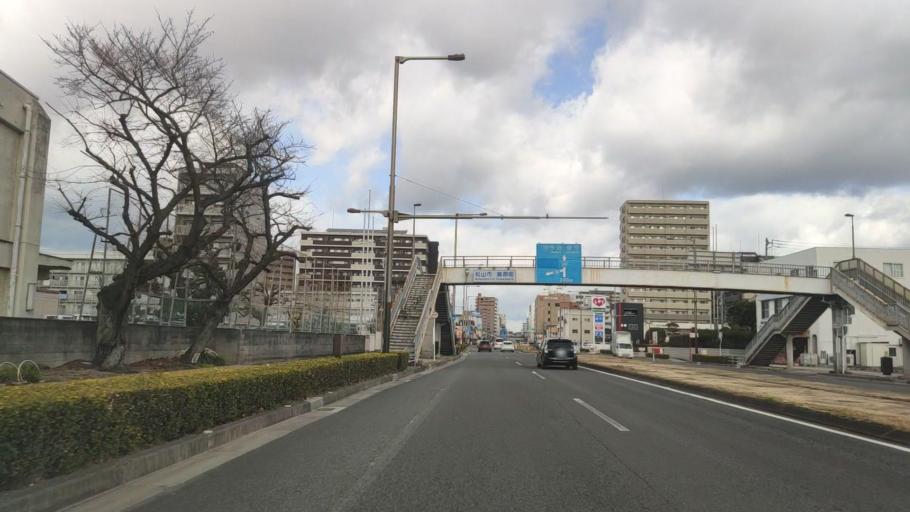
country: JP
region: Ehime
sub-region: Shikoku-chuo Shi
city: Matsuyama
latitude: 33.8315
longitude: 132.7588
